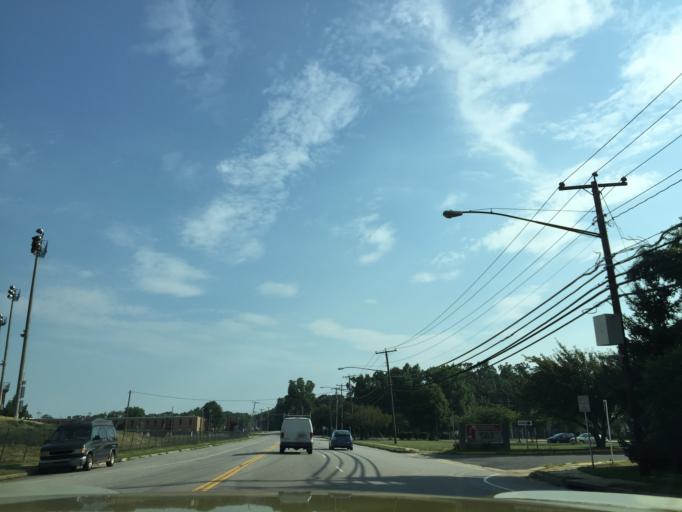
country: US
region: Virginia
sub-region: Fairfax County
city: Mount Vernon
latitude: 38.7305
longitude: -77.0933
